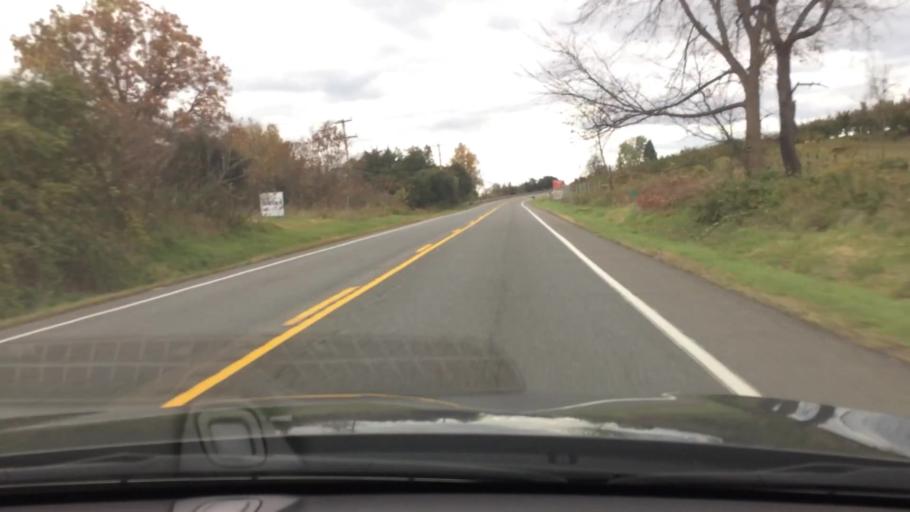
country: US
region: New York
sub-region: Columbia County
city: Stottville
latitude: 42.3159
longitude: -73.7016
